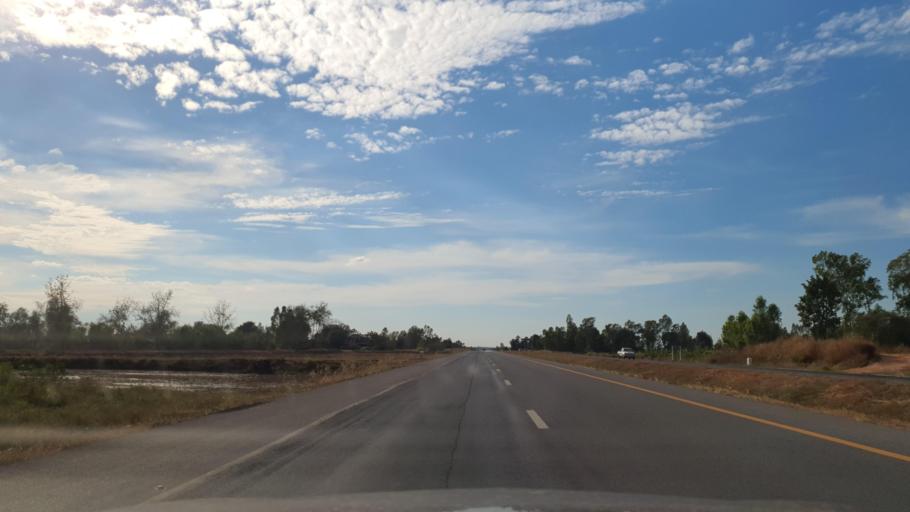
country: TH
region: Roi Et
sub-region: Amphoe Pho Chai
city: Pho Chai
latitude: 16.4136
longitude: 103.7854
